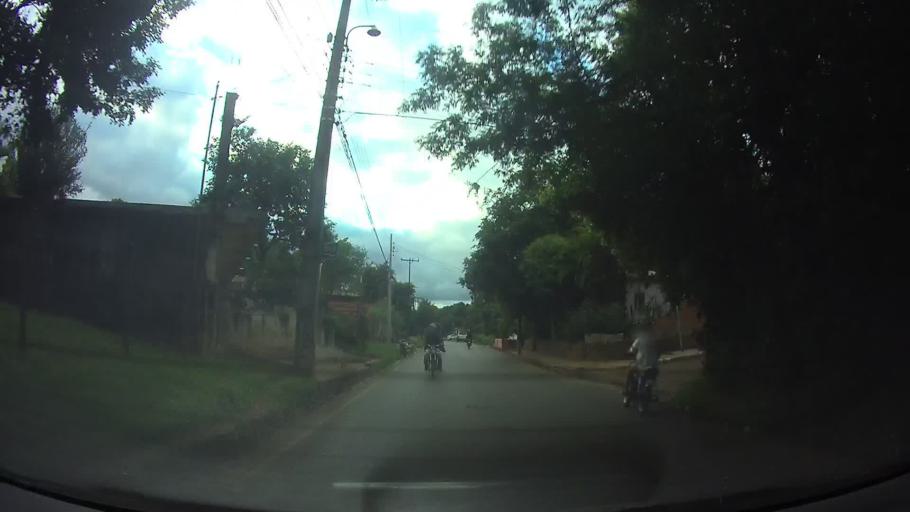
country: PY
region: Central
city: San Lorenzo
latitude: -25.3024
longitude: -57.4967
